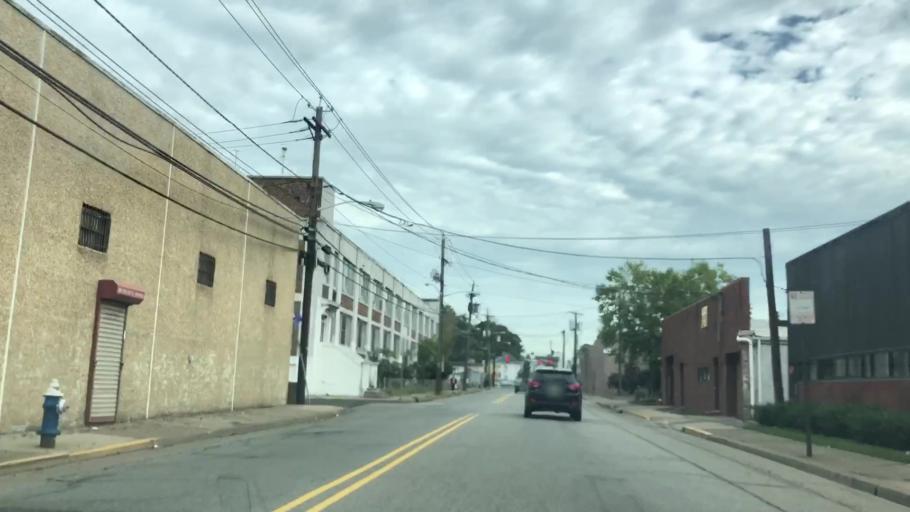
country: US
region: New Jersey
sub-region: Union County
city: Hillside
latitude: 40.7122
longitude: -74.2309
